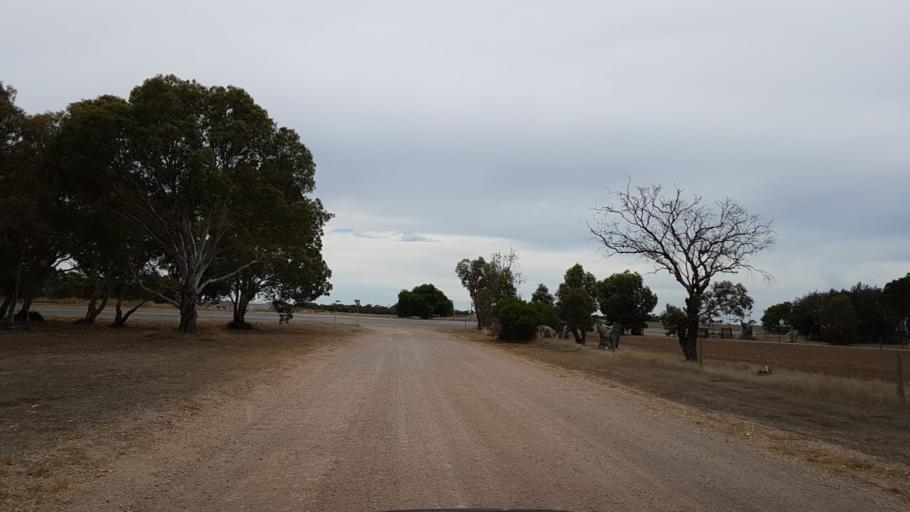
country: AU
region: South Australia
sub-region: Yorke Peninsula
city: Port Victoria
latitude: -34.7741
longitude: 137.6072
